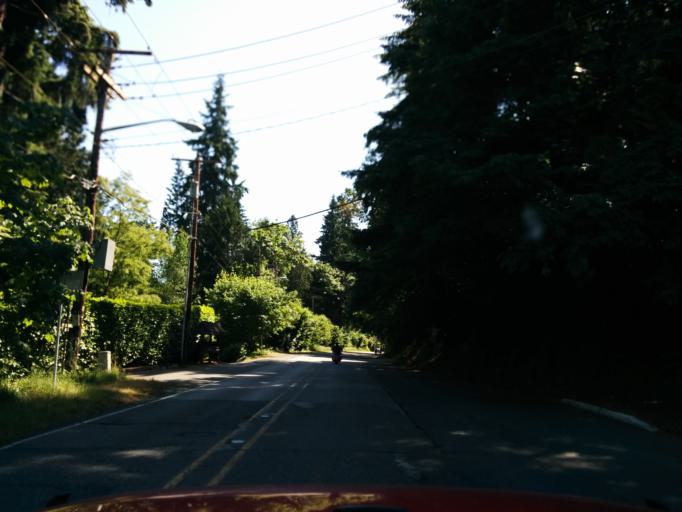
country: US
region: Washington
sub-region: King County
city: West Lake Sammamish
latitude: 47.6102
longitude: -122.1103
